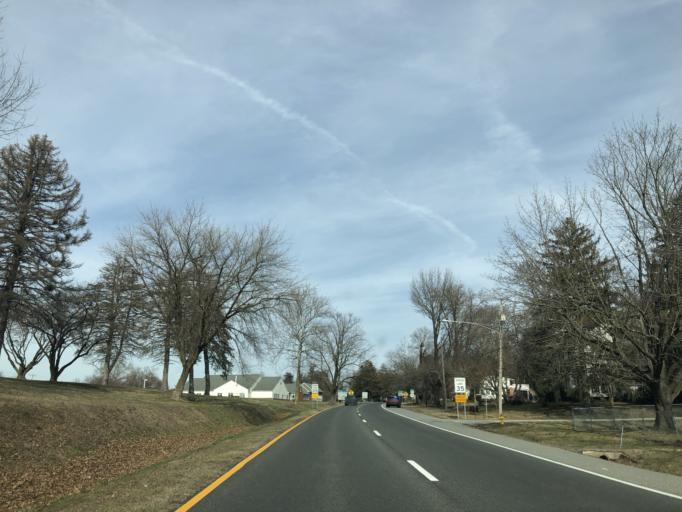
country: US
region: Delaware
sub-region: New Castle County
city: Middletown
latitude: 39.4532
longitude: -75.6634
